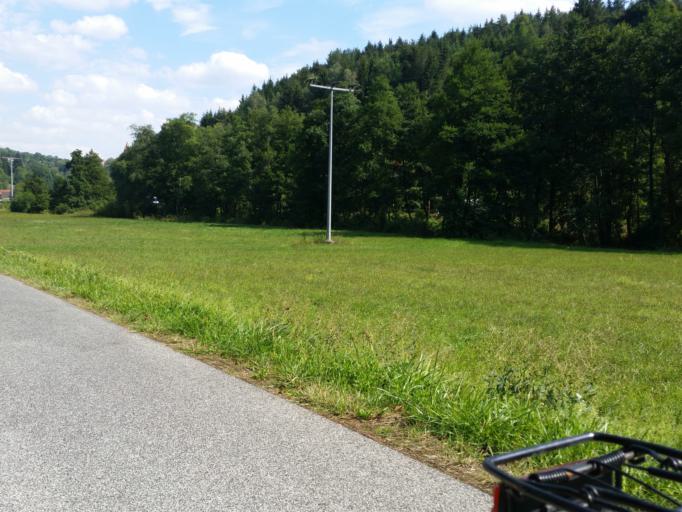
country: DE
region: Bavaria
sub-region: Upper Palatinate
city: Kastl
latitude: 49.3707
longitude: 11.6684
